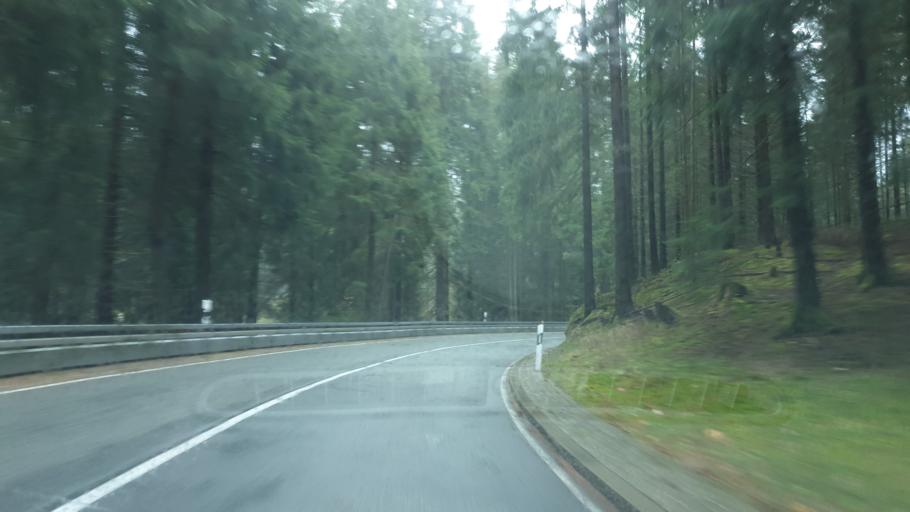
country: DE
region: Saxony
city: Muldenhammer
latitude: 50.4671
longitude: 12.5088
